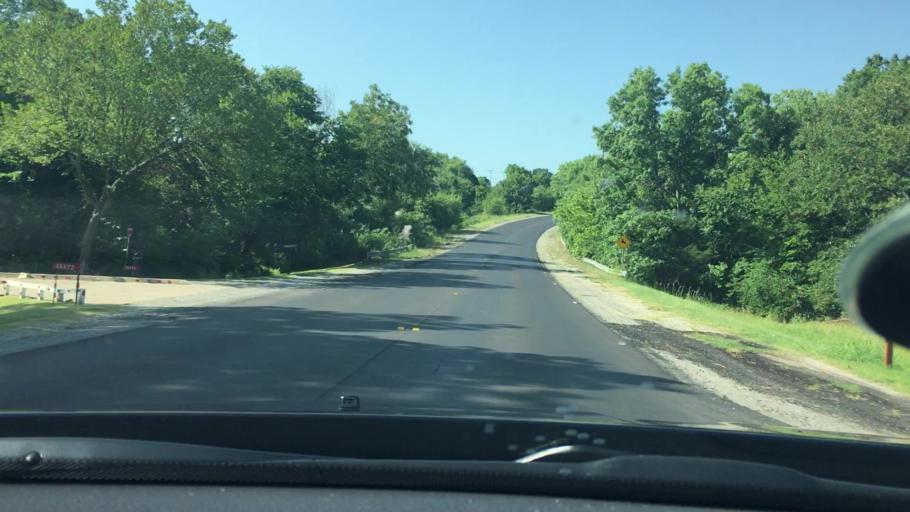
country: US
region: Oklahoma
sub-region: Pontotoc County
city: Ada
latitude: 34.7447
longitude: -96.6702
